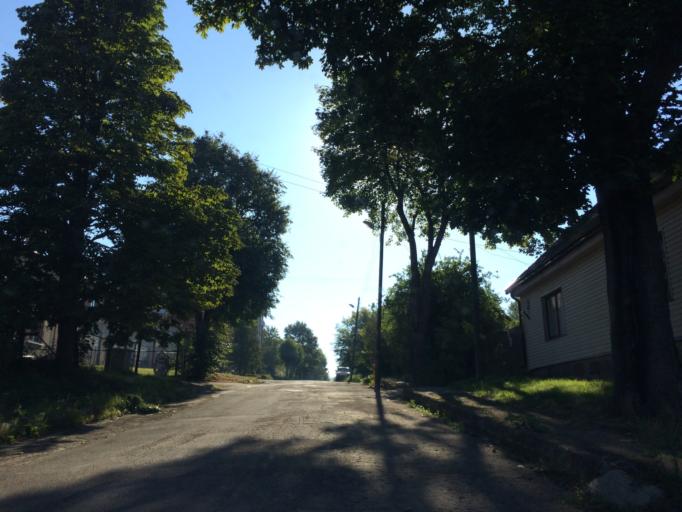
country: LV
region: Rezekne
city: Rezekne
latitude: 56.5119
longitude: 27.3276
